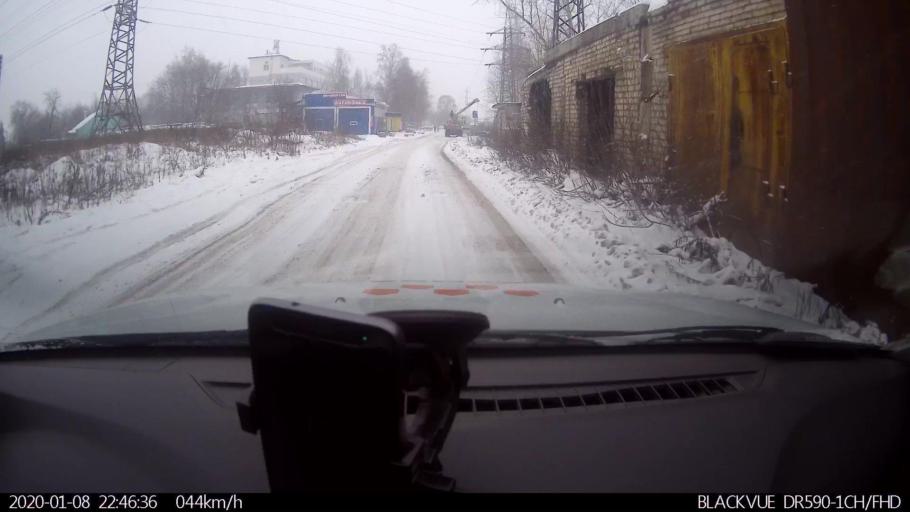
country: RU
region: Nizjnij Novgorod
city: Nizhniy Novgorod
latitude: 56.2949
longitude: 43.8938
